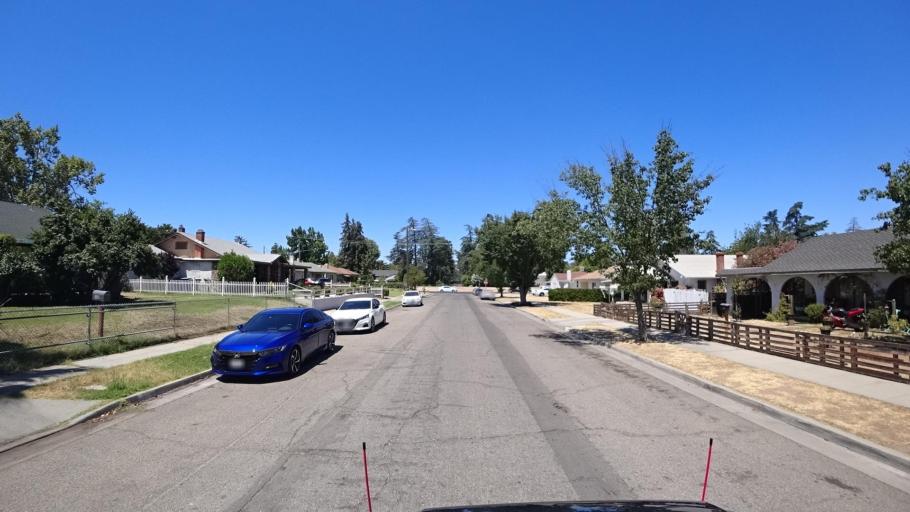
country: US
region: California
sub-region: Fresno County
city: Fresno
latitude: 36.7840
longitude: -119.7985
